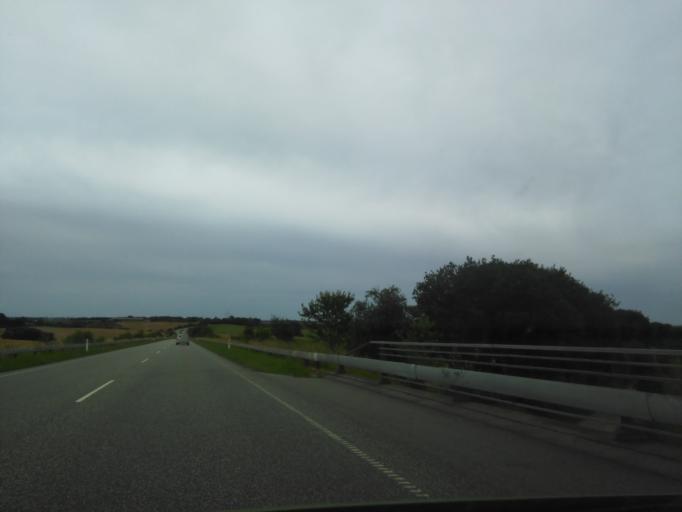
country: DK
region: Central Jutland
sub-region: Horsens Kommune
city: Horsens
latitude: 55.9027
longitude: 9.8845
